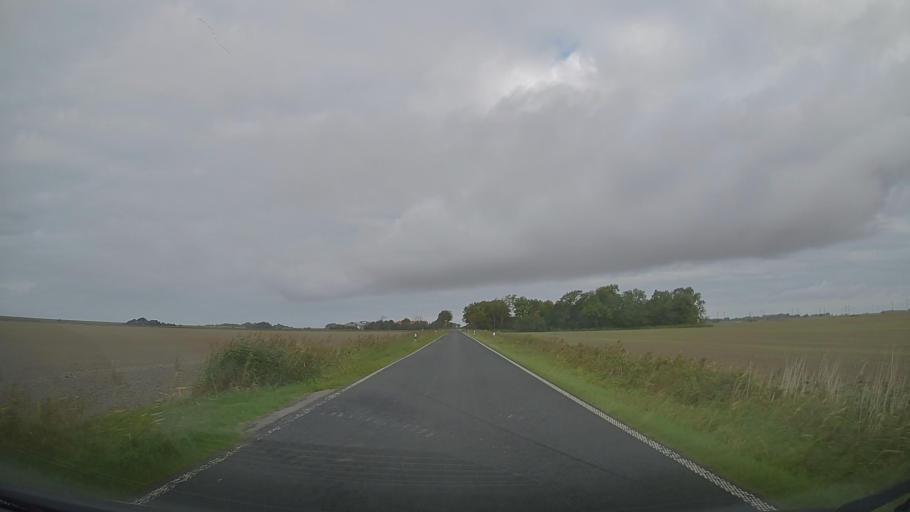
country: DE
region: Schleswig-Holstein
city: Galmsbull
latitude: 54.7513
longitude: 8.7304
